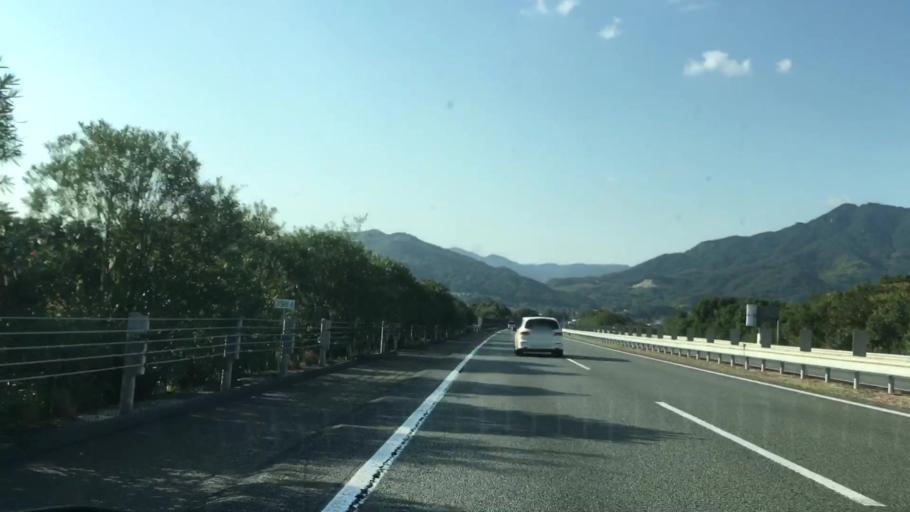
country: JP
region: Yamaguchi
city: Hofu
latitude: 34.0598
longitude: 131.6121
